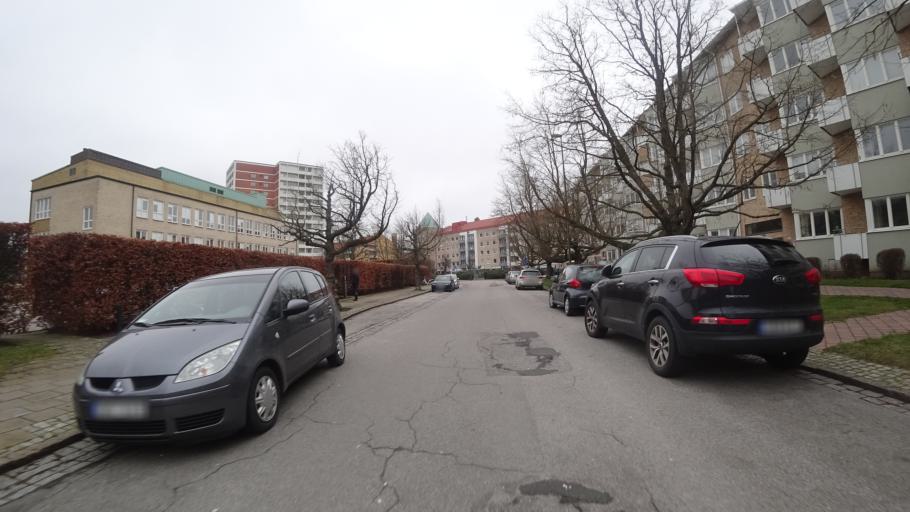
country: SE
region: Skane
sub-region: Malmo
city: Malmoe
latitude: 55.5930
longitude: 12.9884
